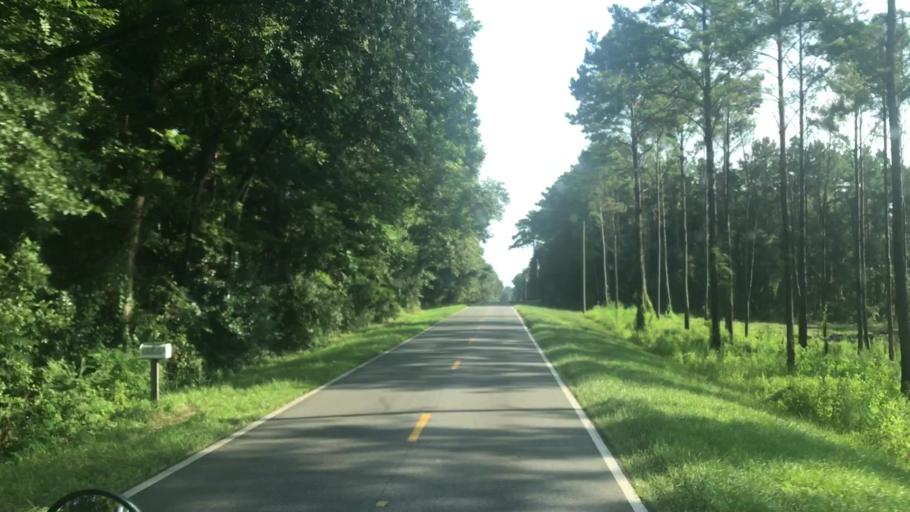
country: US
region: Florida
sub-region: Gadsden County
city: Quincy
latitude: 30.6789
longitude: -84.5407
